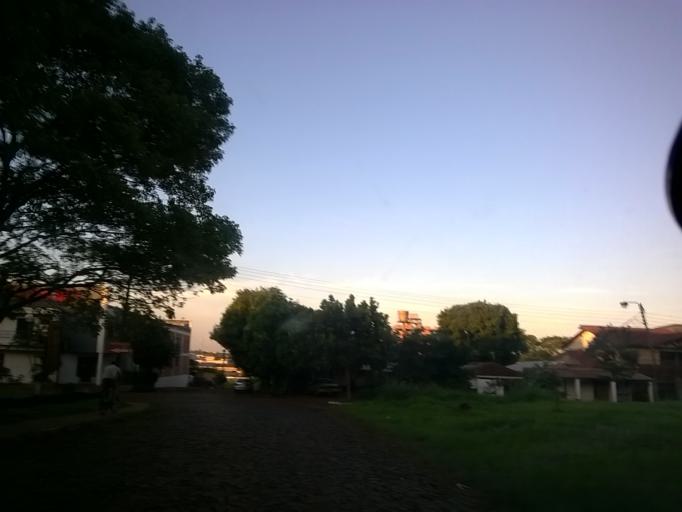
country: PY
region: Alto Parana
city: Ciudad del Este
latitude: -25.5083
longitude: -54.6528
